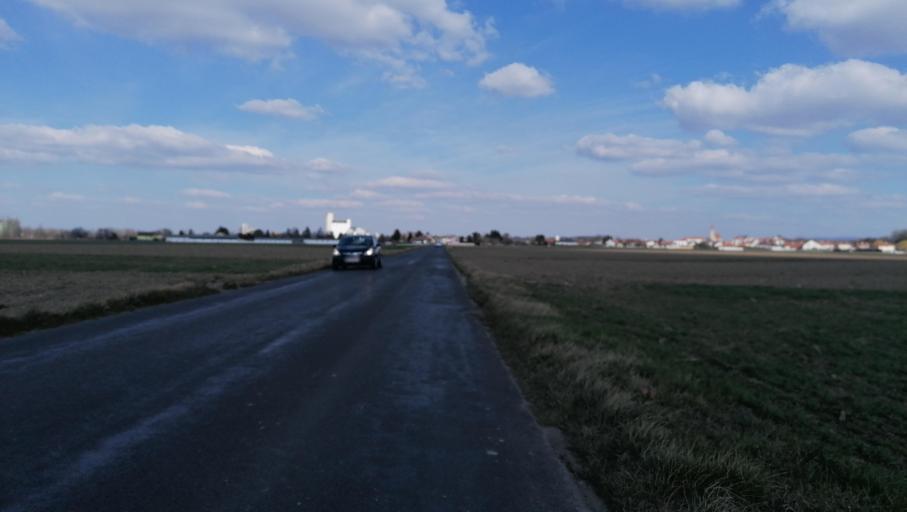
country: AT
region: Lower Austria
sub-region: Politischer Bezirk Wiener Neustadt
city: Lichtenworth
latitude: 47.8276
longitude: 16.2824
